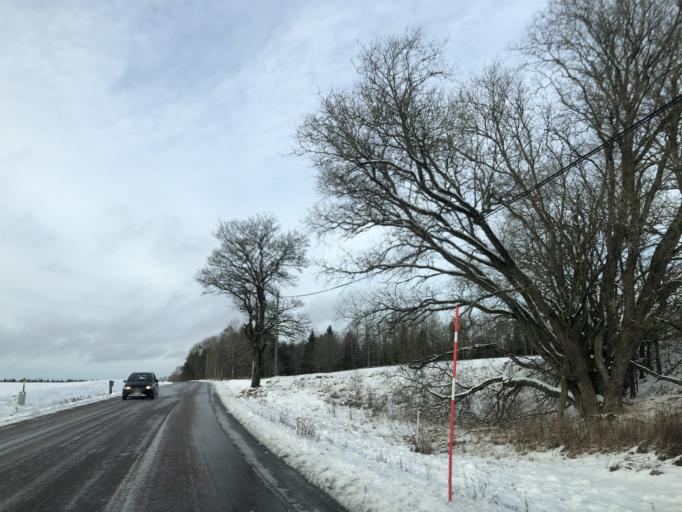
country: SE
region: Vaestra Goetaland
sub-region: Ulricehamns Kommun
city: Ulricehamn
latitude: 57.8121
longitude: 13.5365
